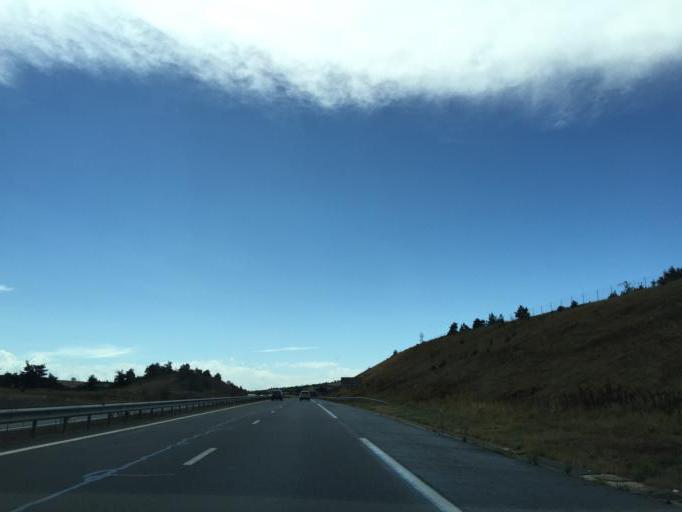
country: FR
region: Midi-Pyrenees
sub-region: Departement de l'Aveyron
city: Severac-le-Chateau
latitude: 44.3003
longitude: 3.1009
